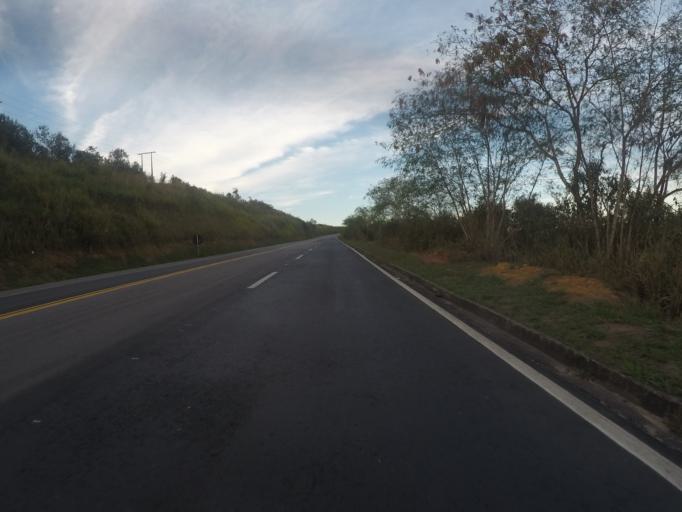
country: BR
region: Espirito Santo
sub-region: Aracruz
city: Aracruz
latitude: -19.6666
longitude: -40.2523
